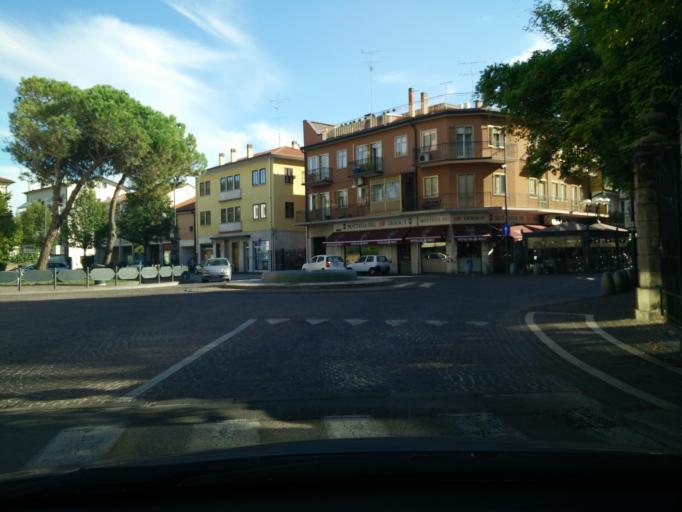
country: IT
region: Veneto
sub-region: Provincia di Venezia
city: San Dona di Piave
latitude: 45.6321
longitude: 12.5660
